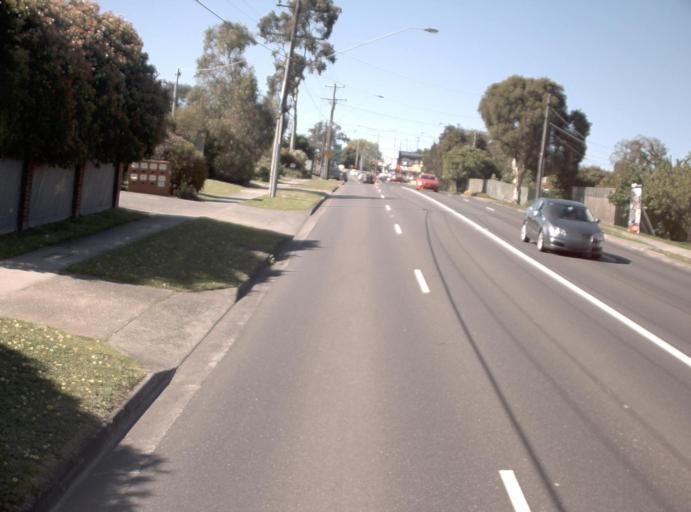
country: AU
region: Victoria
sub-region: Knox
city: Bayswater
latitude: -37.8623
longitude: 145.2661
